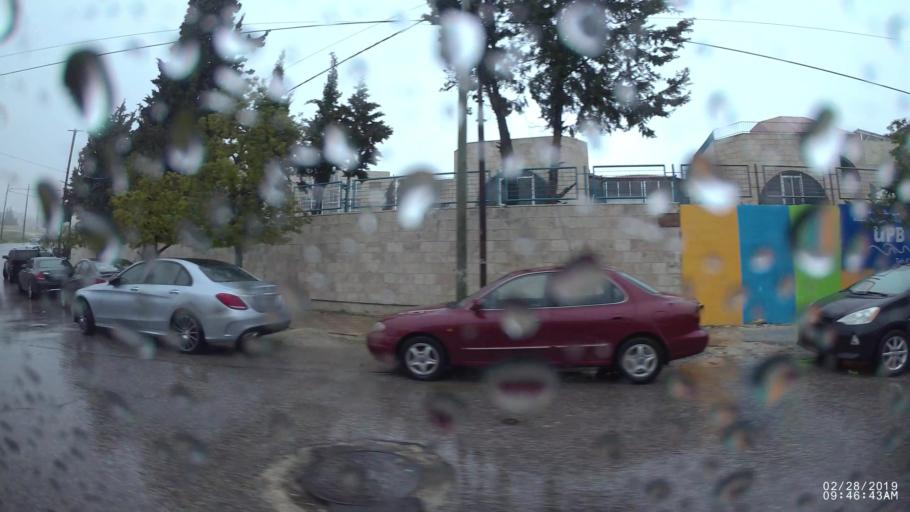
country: JO
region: Amman
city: Al Jubayhah
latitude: 32.0146
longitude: 35.8845
